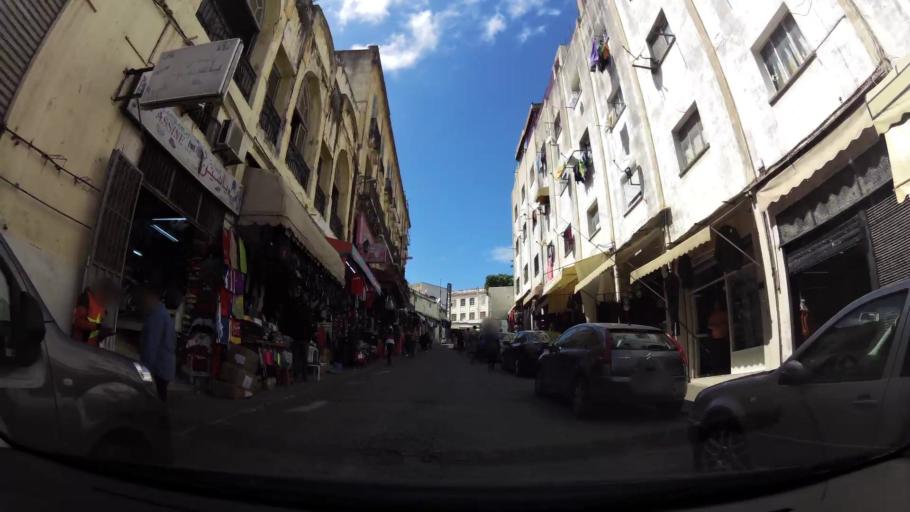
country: MA
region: Tanger-Tetouan
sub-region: Tanger-Assilah
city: Tangier
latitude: 35.7831
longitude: -5.8106
